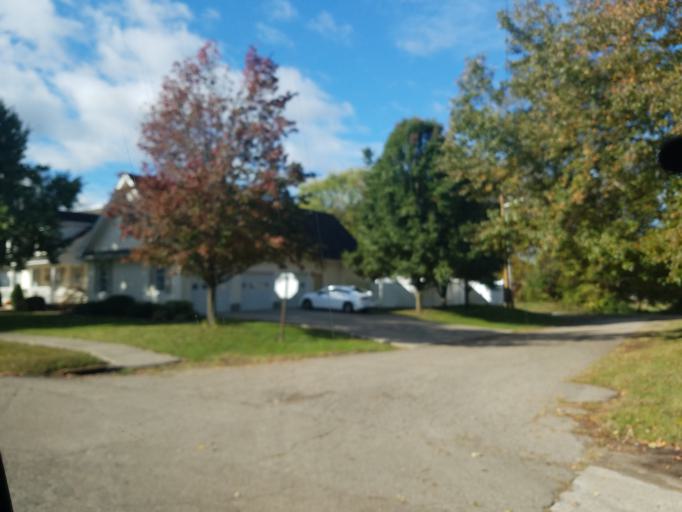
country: US
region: Ohio
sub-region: Jackson County
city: Wellston
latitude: 39.1264
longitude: -82.5339
